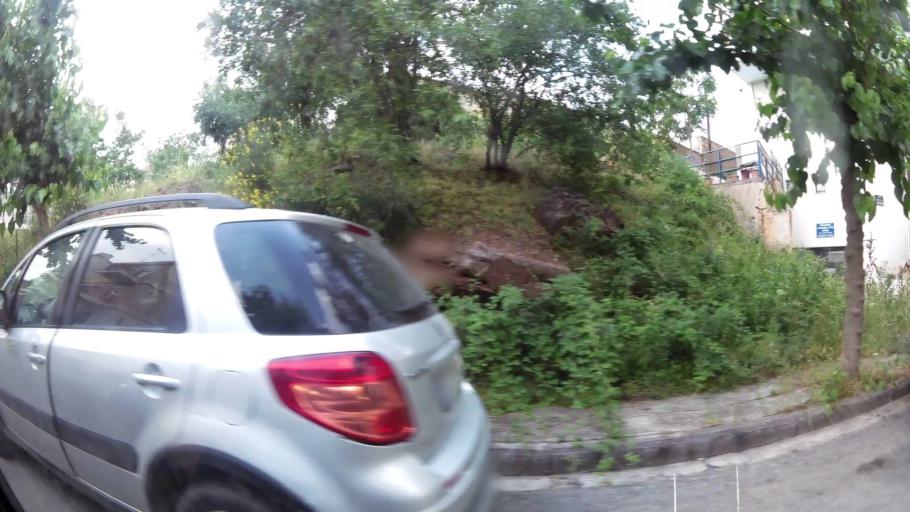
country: GR
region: West Macedonia
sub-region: Nomos Kozanis
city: Kozani
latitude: 40.3079
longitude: 21.7910
